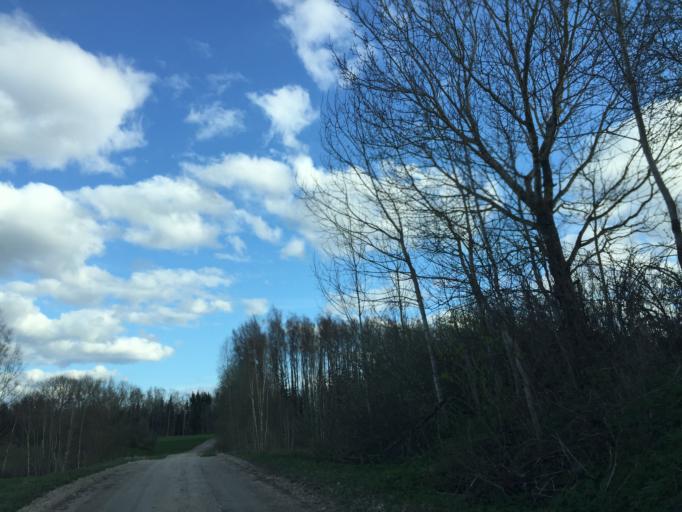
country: LV
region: Karsava
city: Karsava
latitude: 56.6759
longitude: 27.5285
